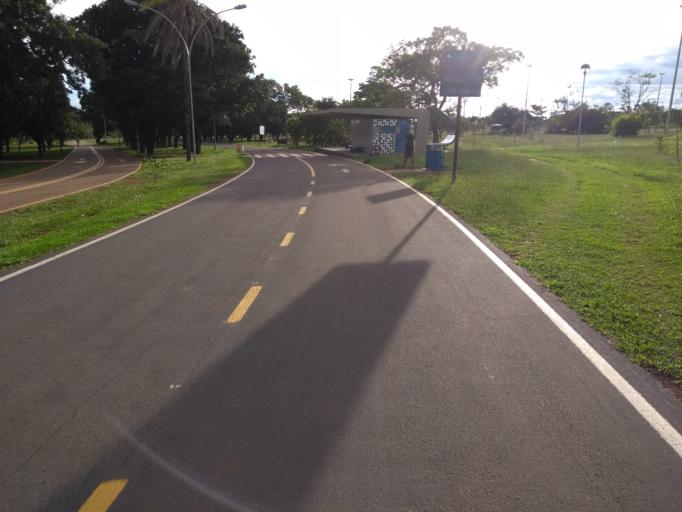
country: BR
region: Federal District
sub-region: Brasilia
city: Brasilia
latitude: -15.8093
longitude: -47.9195
